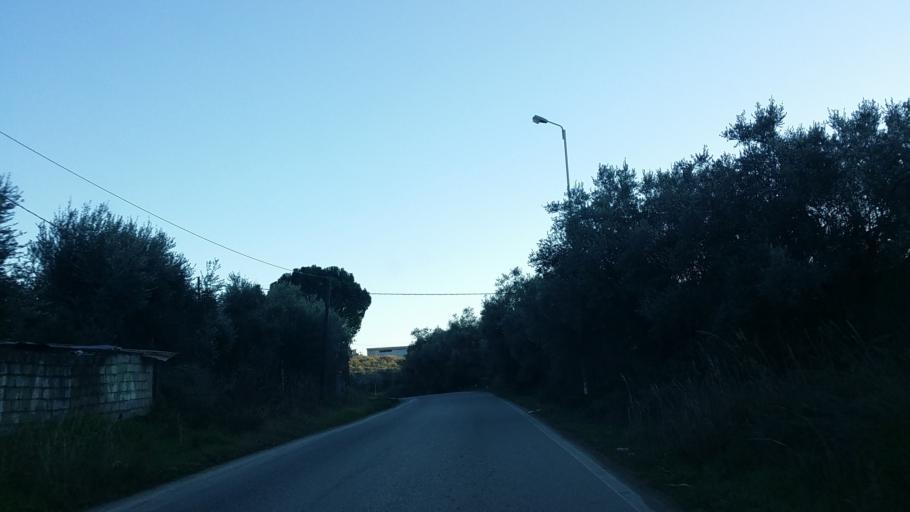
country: GR
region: West Greece
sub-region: Nomos Aitolias kai Akarnanias
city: Neapolis
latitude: 38.6980
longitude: 21.3532
